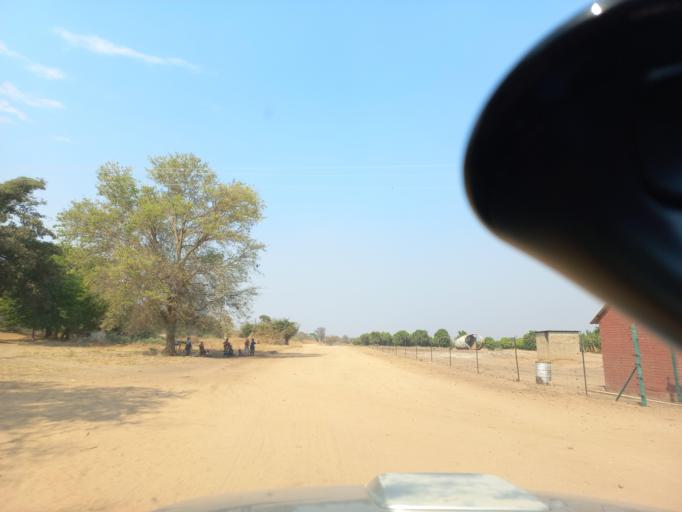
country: ZW
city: Chirundu
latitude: -15.9322
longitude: 28.9500
